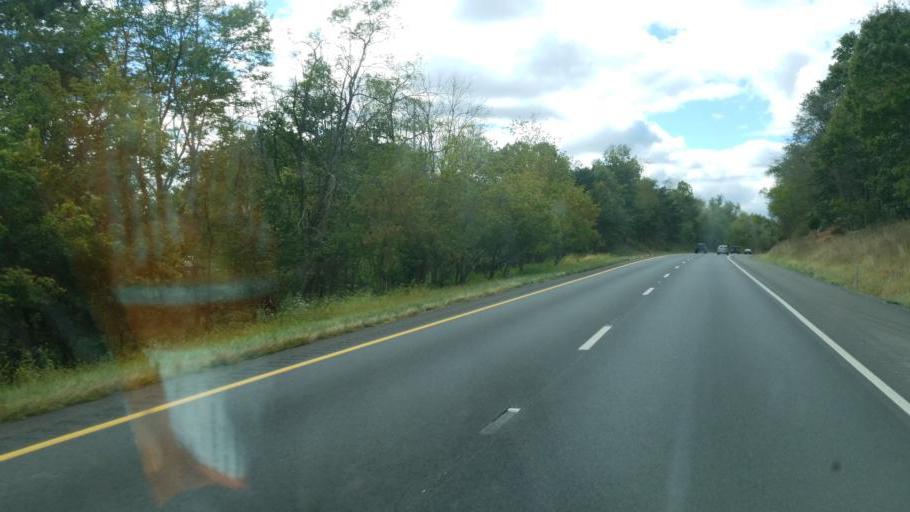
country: US
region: Maryland
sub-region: Washington County
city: Wilson-Conococheague
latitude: 39.6244
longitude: -77.9993
